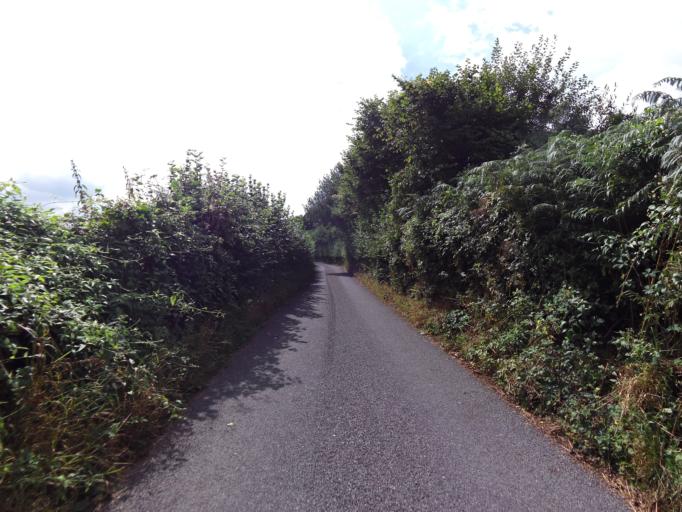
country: GB
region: England
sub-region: Hertfordshire
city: Shenley AV
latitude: 51.7005
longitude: -0.2547
